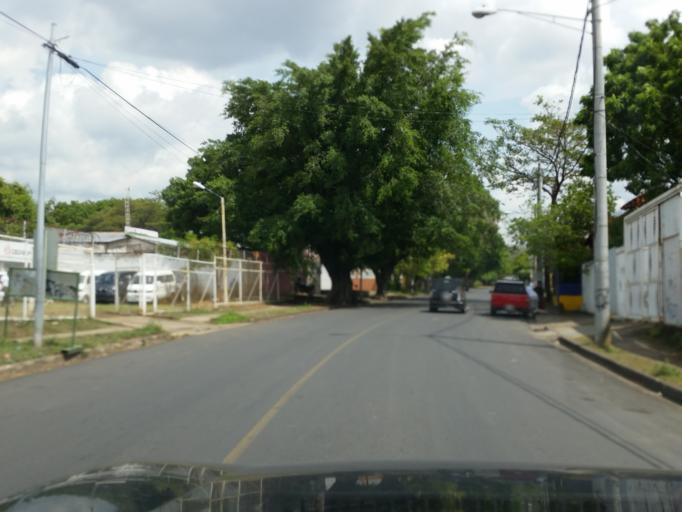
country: NI
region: Managua
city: Ciudad Sandino
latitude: 12.1428
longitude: -86.2995
